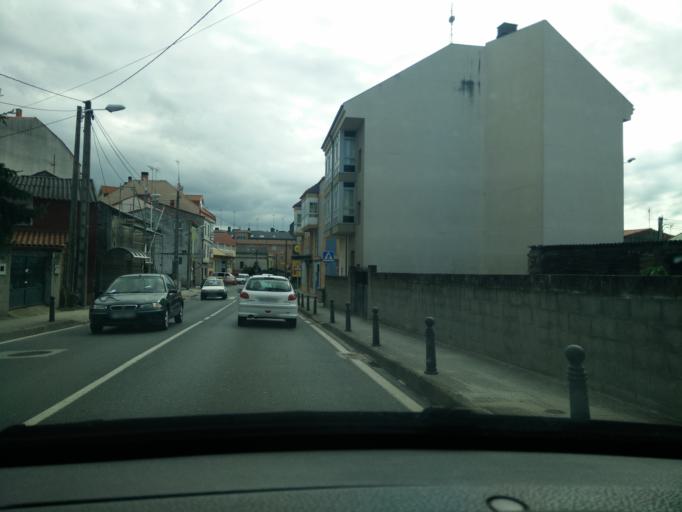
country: ES
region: Galicia
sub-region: Provincia da Coruna
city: A Coruna
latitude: 43.3320
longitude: -8.4252
